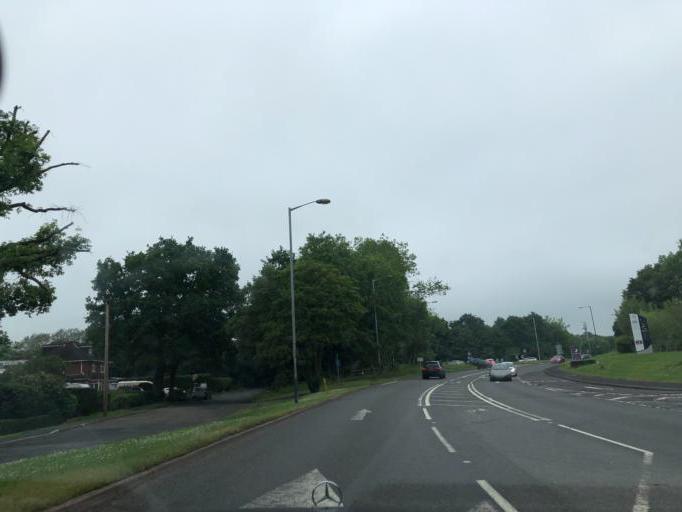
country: GB
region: England
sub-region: Warwickshire
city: Warwick
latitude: 52.2887
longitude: -1.6075
